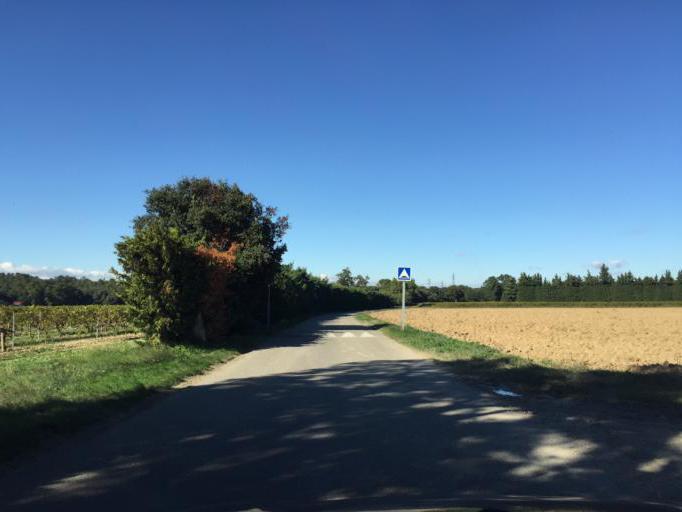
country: FR
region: Provence-Alpes-Cote d'Azur
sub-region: Departement du Vaucluse
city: Piolenc
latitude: 44.1670
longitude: 4.7901
